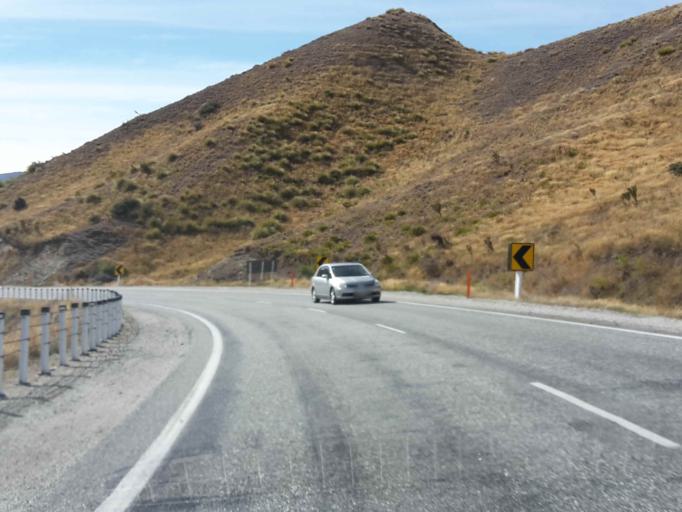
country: NZ
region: Otago
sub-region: Queenstown-Lakes District
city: Wanaka
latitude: -44.5843
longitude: 169.6511
